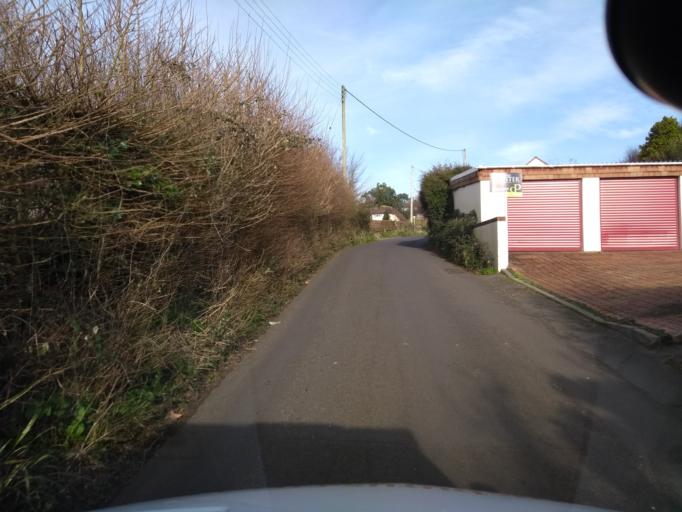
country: GB
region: England
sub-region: North Somerset
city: Bleadon
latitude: 51.3095
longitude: -2.9476
